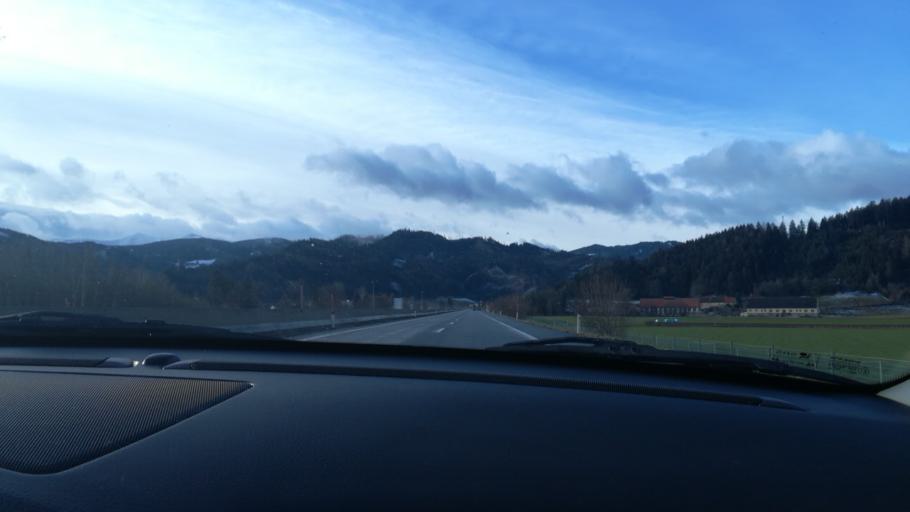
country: AT
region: Styria
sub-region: Politischer Bezirk Murtal
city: Judenburg
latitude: 47.1798
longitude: 14.6643
